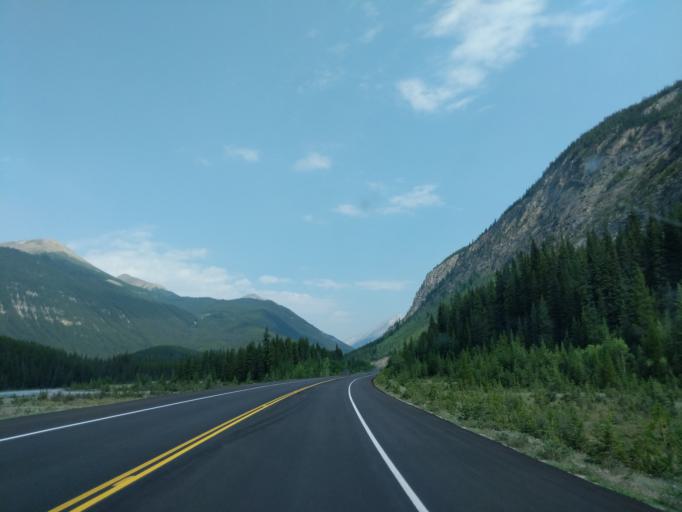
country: CA
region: British Columbia
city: Golden
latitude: 52.1079
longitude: -116.9680
